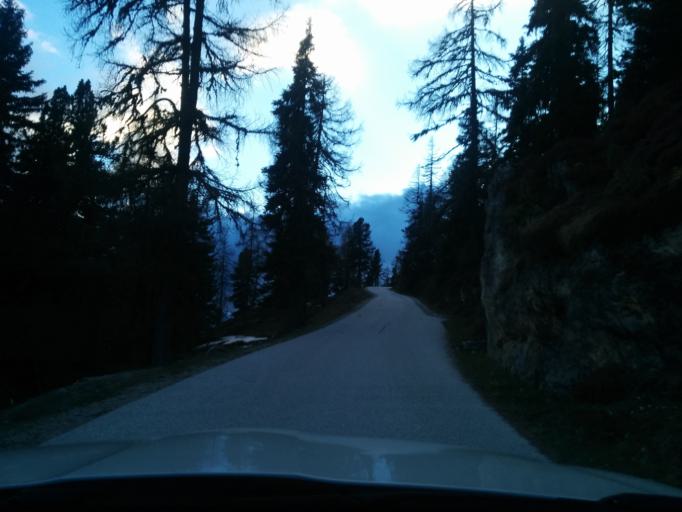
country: AT
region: Styria
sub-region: Politischer Bezirk Liezen
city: Aich
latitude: 47.4560
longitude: 13.8122
